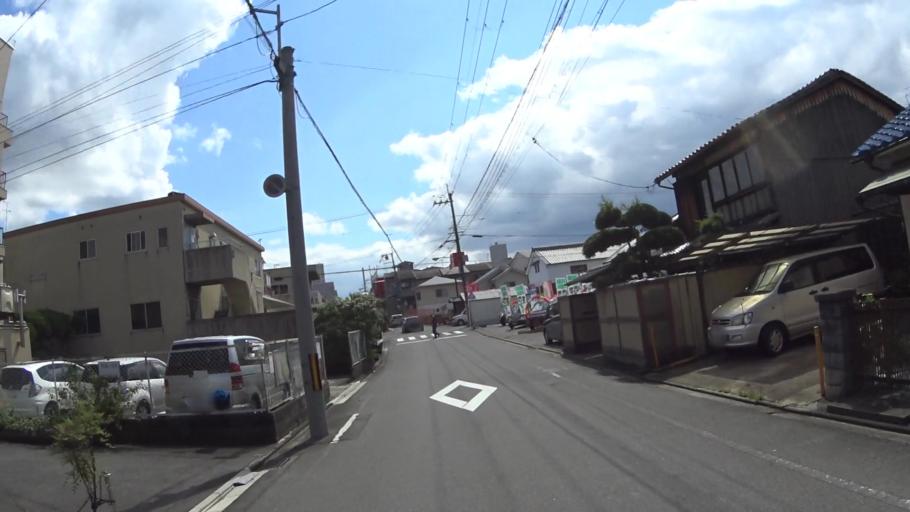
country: JP
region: Kyoto
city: Muko
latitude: 34.9378
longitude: 135.7575
